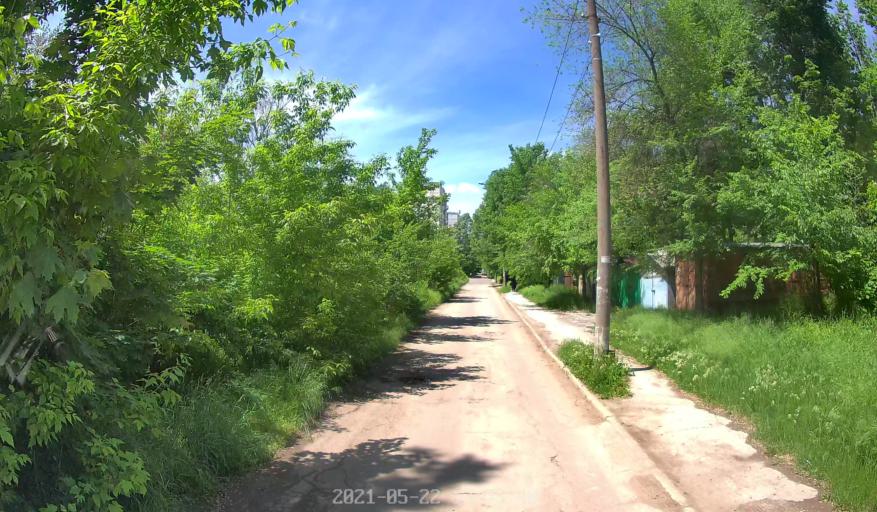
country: MD
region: Chisinau
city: Chisinau
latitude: 47.0559
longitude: 28.8198
